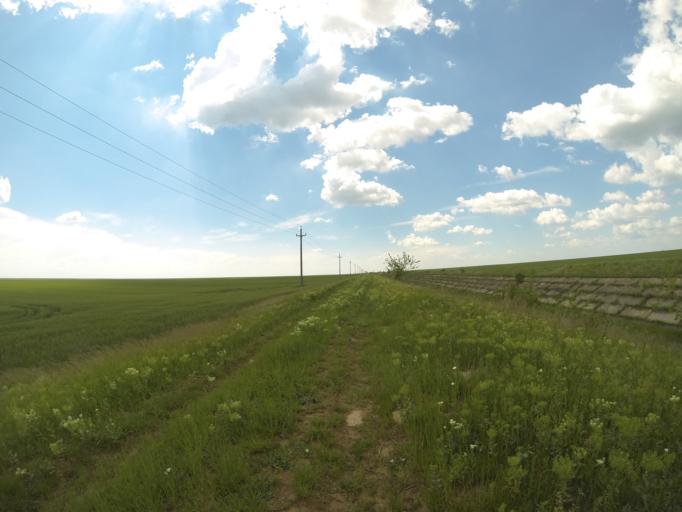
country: RO
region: Dolj
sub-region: Comuna Dranicu
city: Dranic
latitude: 44.0146
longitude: 23.8065
